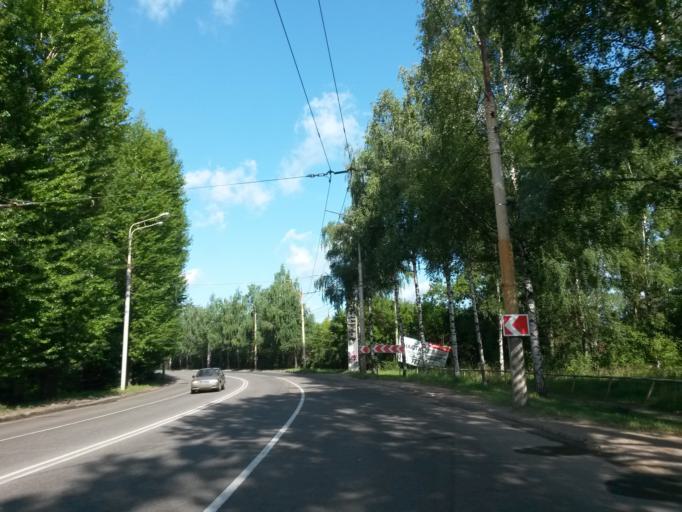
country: RU
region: Jaroslavl
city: Yaroslavl
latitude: 57.6606
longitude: 39.8602
